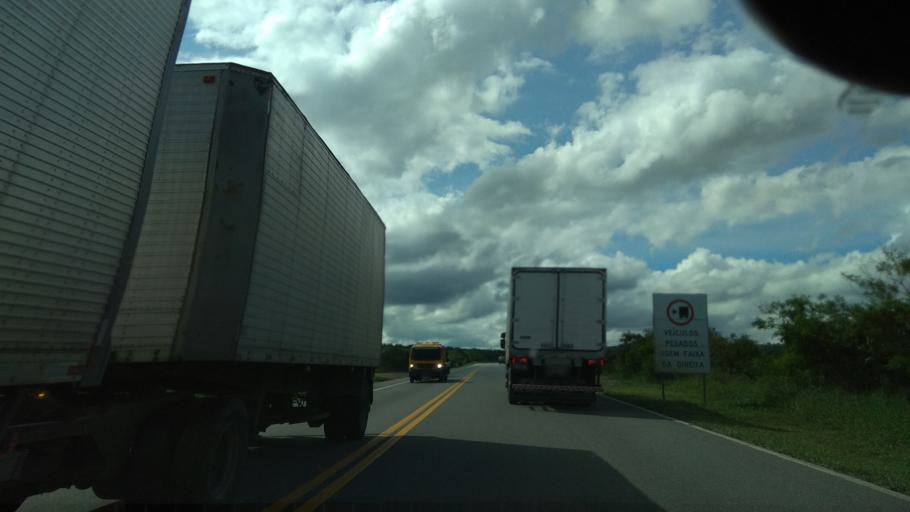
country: BR
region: Bahia
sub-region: Santa Ines
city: Santa Ines
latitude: -13.1333
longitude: -39.9942
